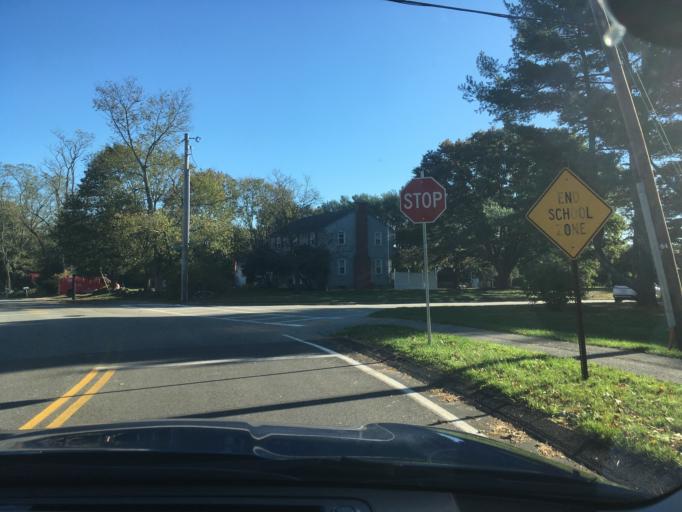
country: US
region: Rhode Island
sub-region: Kent County
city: East Greenwich
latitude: 41.6517
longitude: -71.4677
